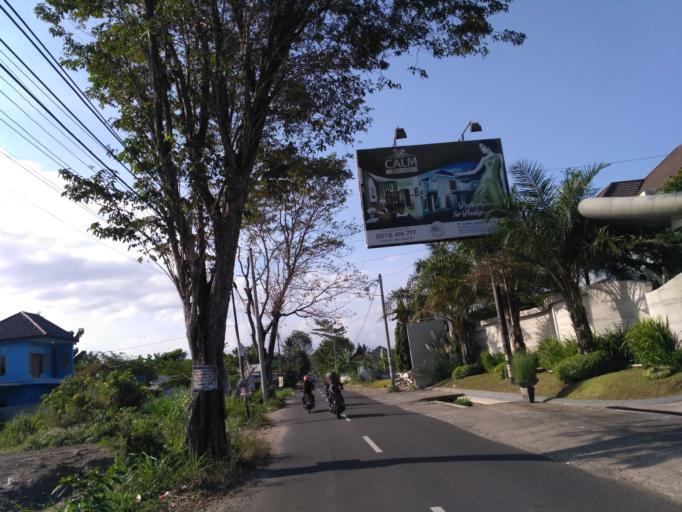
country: ID
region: Daerah Istimewa Yogyakarta
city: Depok
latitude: -7.7787
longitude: 110.4232
